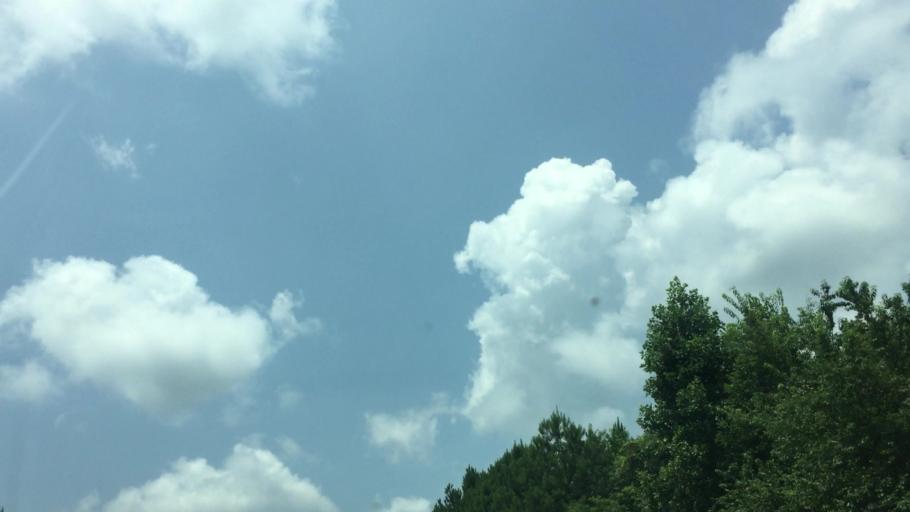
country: US
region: Georgia
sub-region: Fulton County
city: Chattahoochee Hills
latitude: 33.5626
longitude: -84.7719
